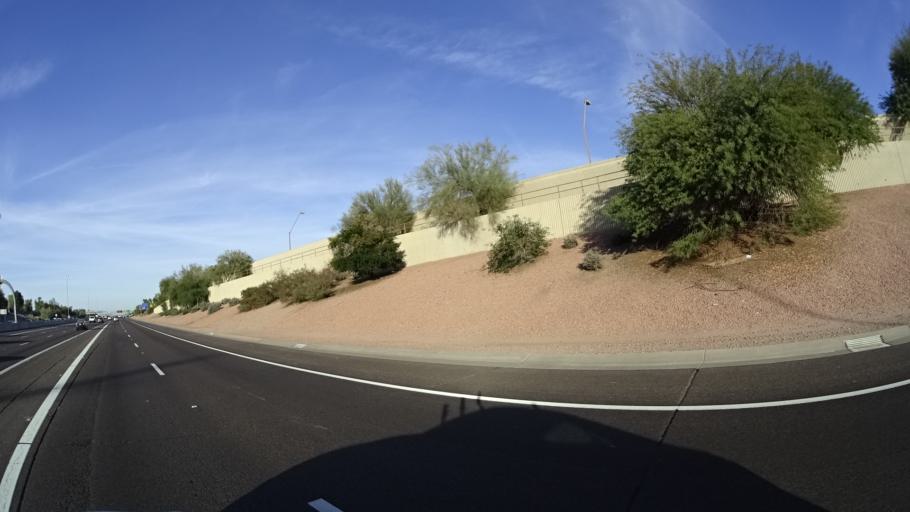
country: US
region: Arizona
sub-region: Maricopa County
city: Tempe
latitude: 33.3937
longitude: -111.8909
